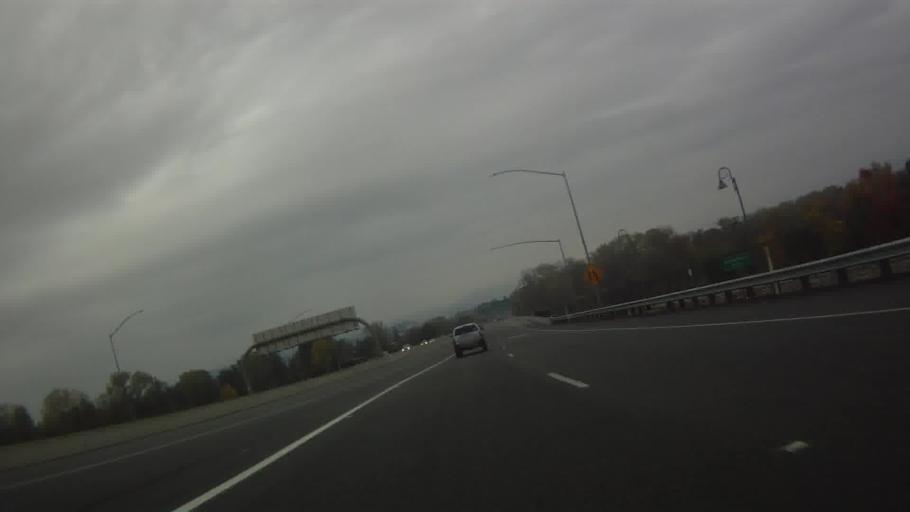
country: US
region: California
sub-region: Shasta County
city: Redding
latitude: 40.5859
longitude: -122.3653
